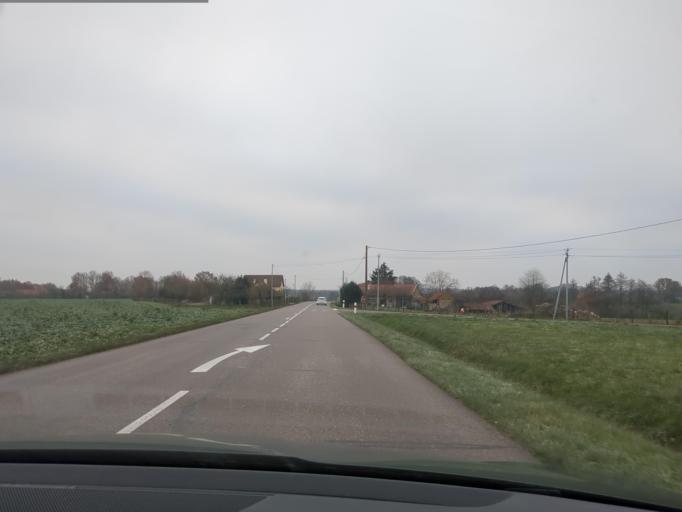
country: FR
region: Bourgogne
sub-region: Departement de Saone-et-Loire
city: Mervans
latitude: 46.7467
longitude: 5.1547
